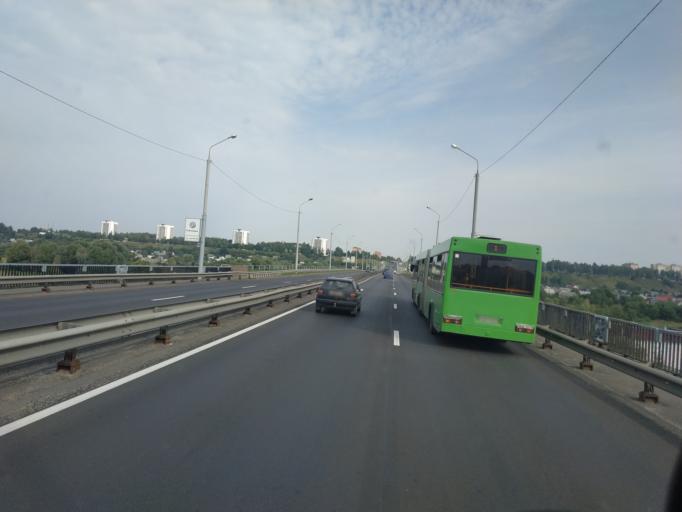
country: BY
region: Mogilev
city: Mahilyow
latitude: 53.8928
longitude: 30.3742
